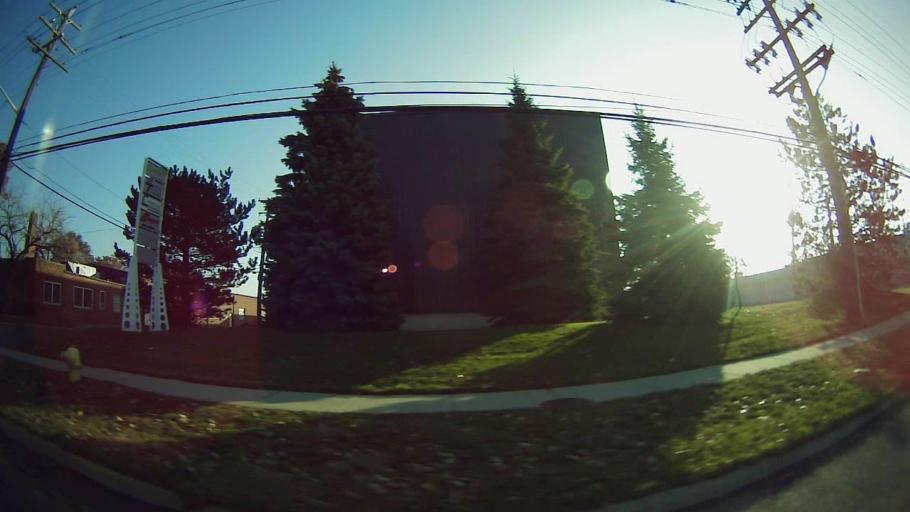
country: US
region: Michigan
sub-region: Oakland County
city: Oak Park
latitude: 42.4543
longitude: -83.1618
